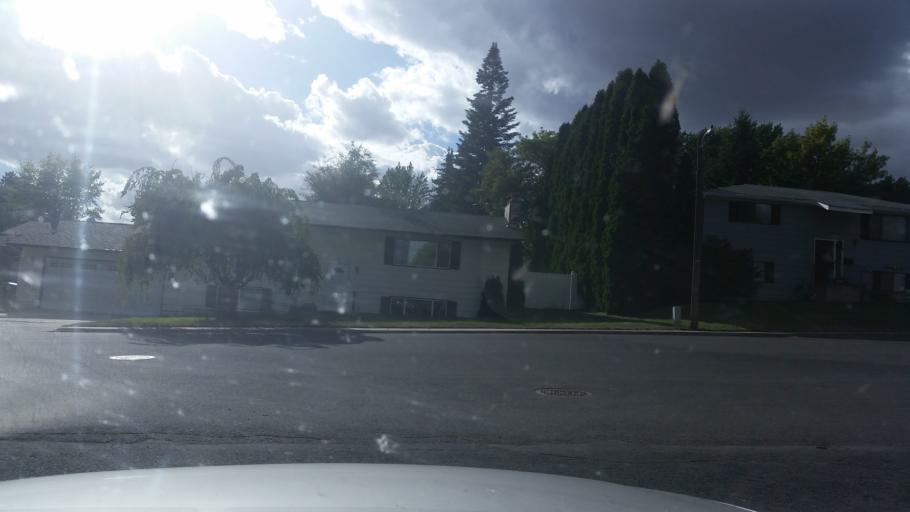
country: US
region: Washington
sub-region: Spokane County
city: Cheney
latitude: 47.4827
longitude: -117.5966
